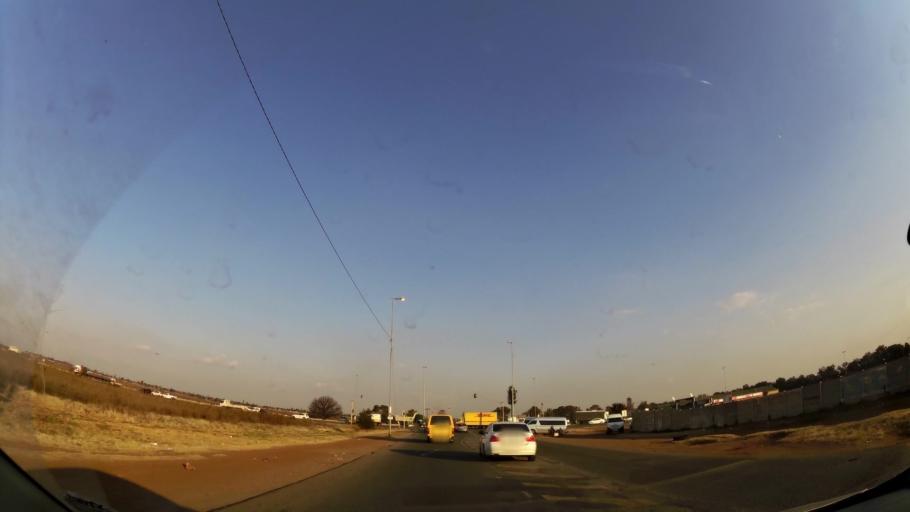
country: ZA
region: Gauteng
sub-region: Ekurhuleni Metropolitan Municipality
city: Germiston
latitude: -26.2889
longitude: 28.2289
